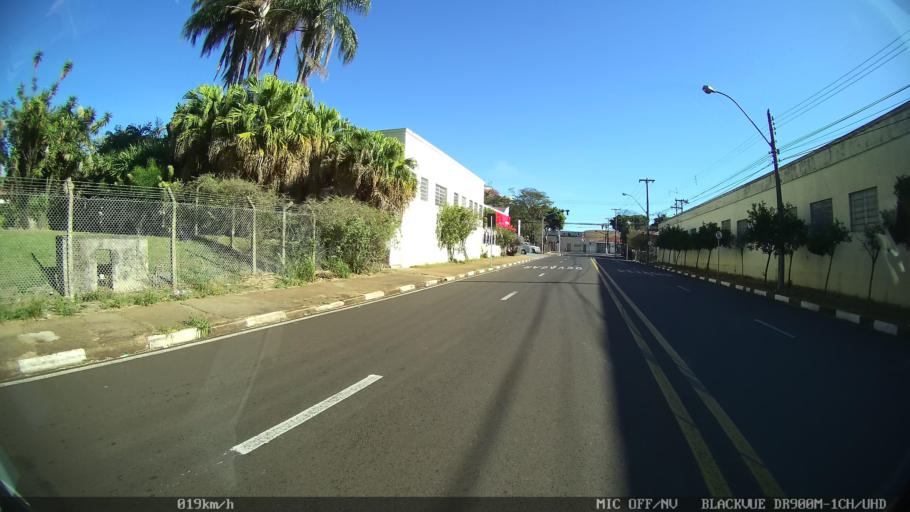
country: BR
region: Sao Paulo
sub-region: Franca
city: Franca
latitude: -20.5396
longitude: -47.4150
